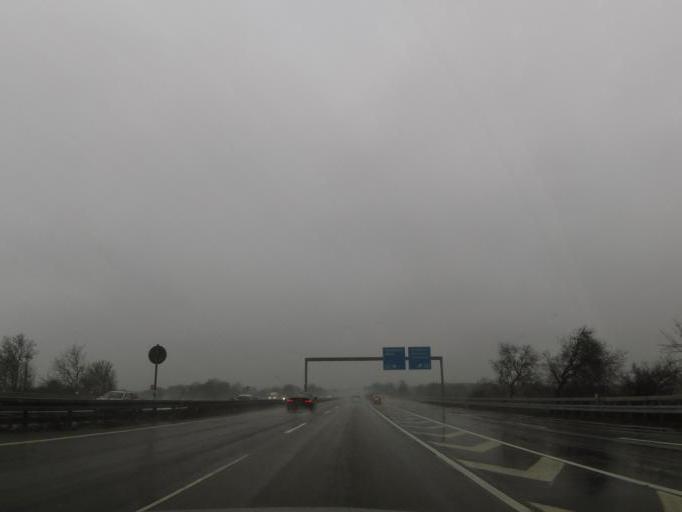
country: DE
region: Hesse
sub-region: Regierungsbezirk Darmstadt
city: Florsheim
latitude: 50.0517
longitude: 8.3914
